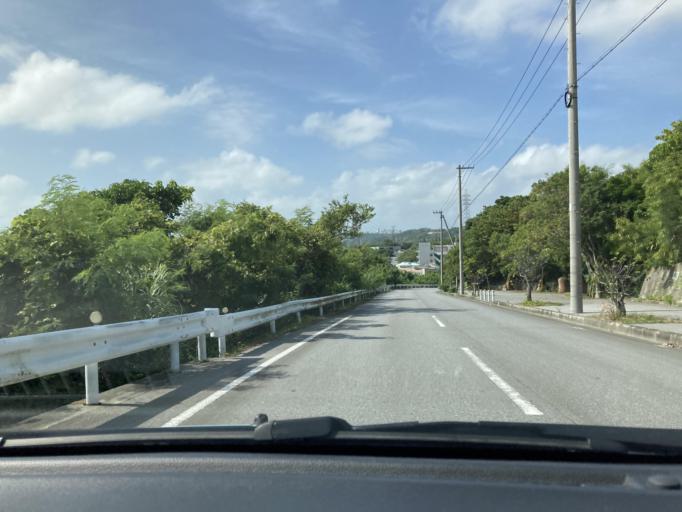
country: JP
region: Okinawa
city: Ginowan
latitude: 26.2791
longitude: 127.7990
